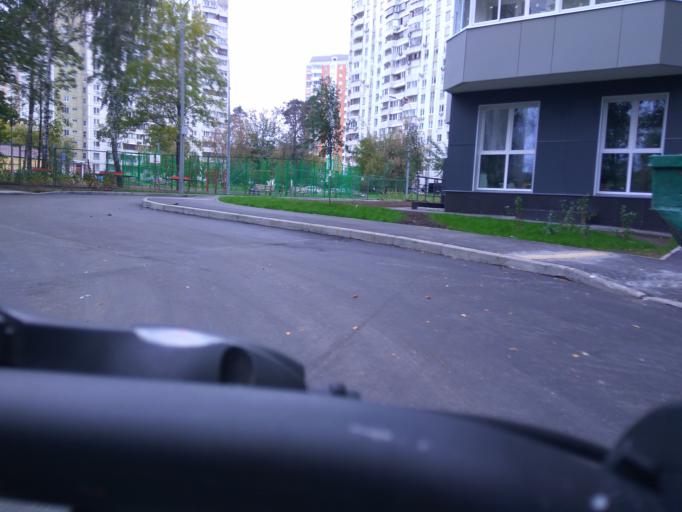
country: RU
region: Moscow
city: Sviblovo
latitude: 55.8566
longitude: 37.6389
